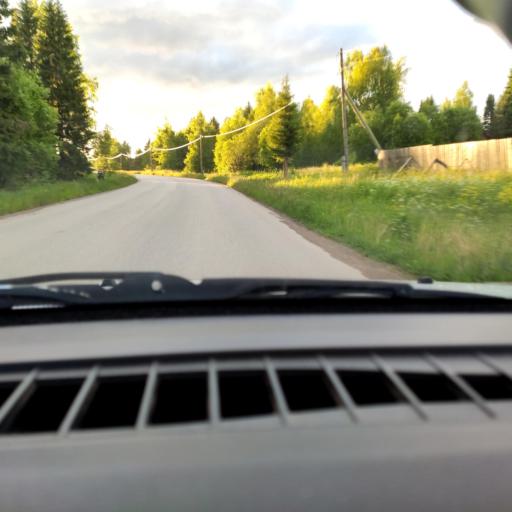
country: RU
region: Perm
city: Polazna
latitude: 58.2102
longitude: 56.5135
